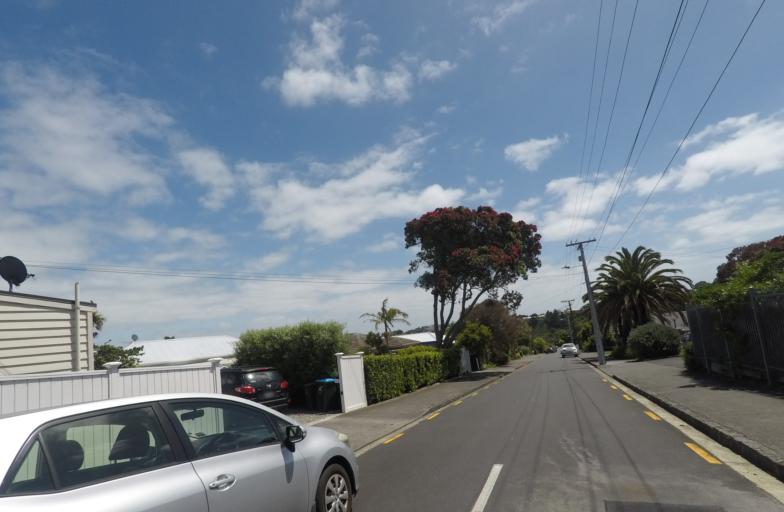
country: NZ
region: Auckland
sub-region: Auckland
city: Auckland
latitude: -36.8728
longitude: 174.7377
